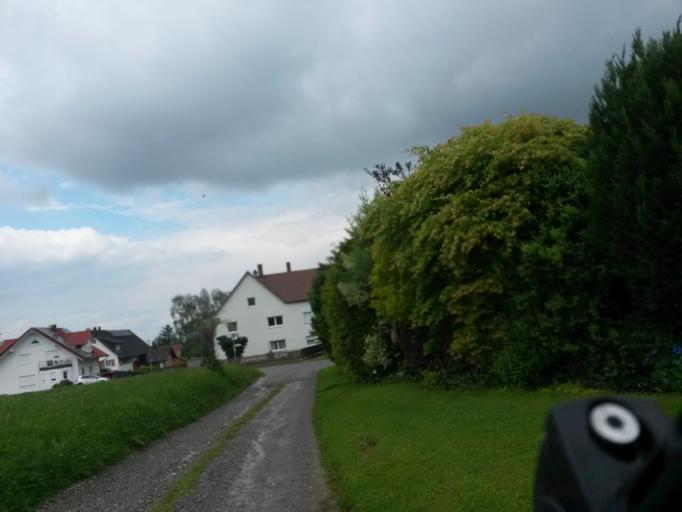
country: DE
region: Baden-Wuerttemberg
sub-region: Tuebingen Region
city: Bad Wurzach
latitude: 47.9300
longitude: 9.8373
